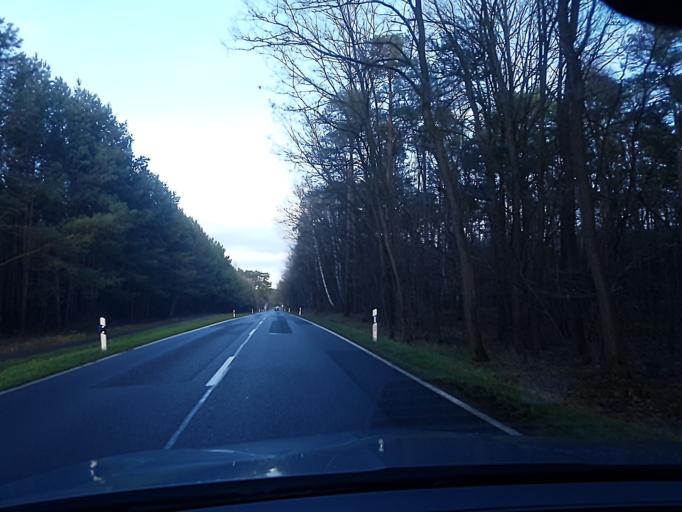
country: DE
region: Brandenburg
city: Trobitz
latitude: 51.5703
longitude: 13.4225
